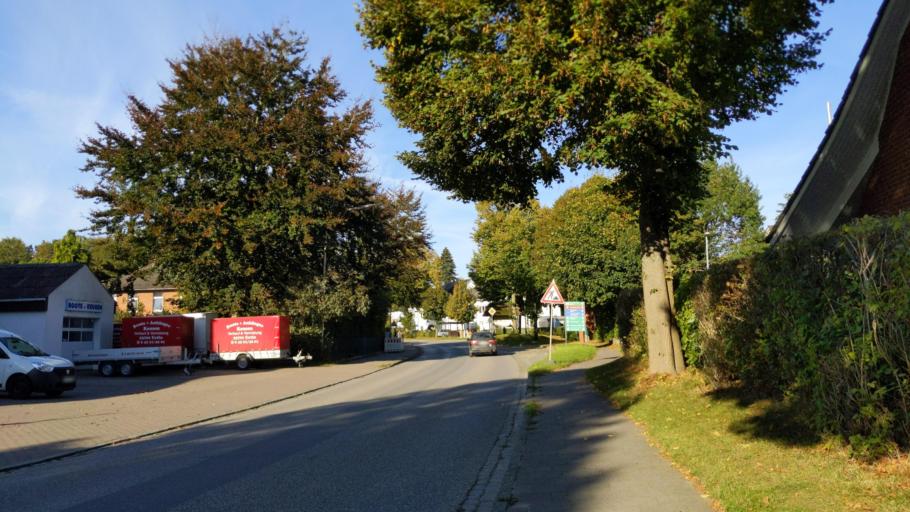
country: DE
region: Schleswig-Holstein
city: Eutin
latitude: 54.1515
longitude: 10.6088
